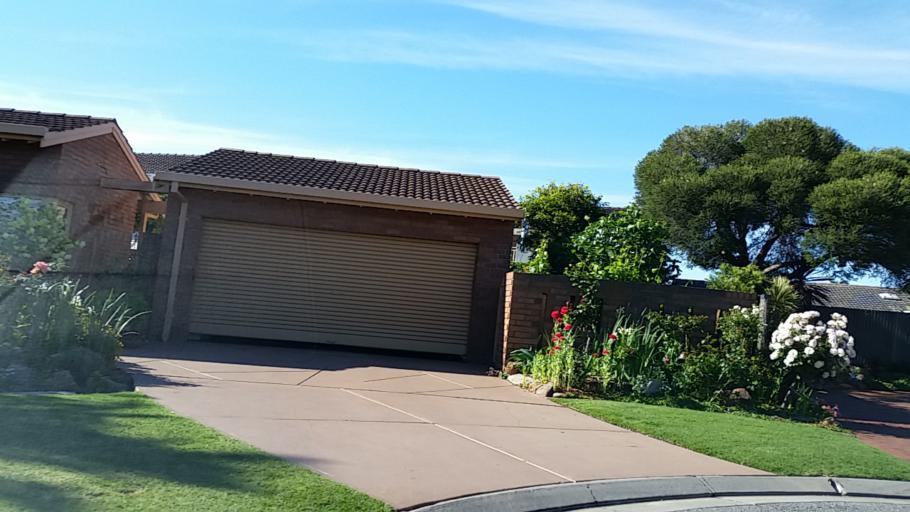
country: AU
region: South Australia
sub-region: Charles Sturt
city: West Lakes Shore
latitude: -34.8642
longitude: 138.4911
